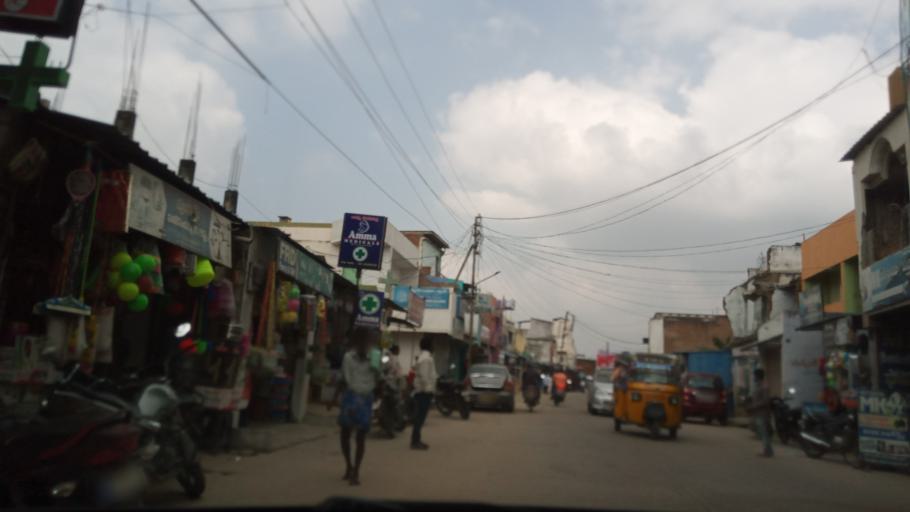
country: IN
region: Andhra Pradesh
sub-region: Chittoor
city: Madanapalle
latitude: 13.6370
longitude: 78.6296
